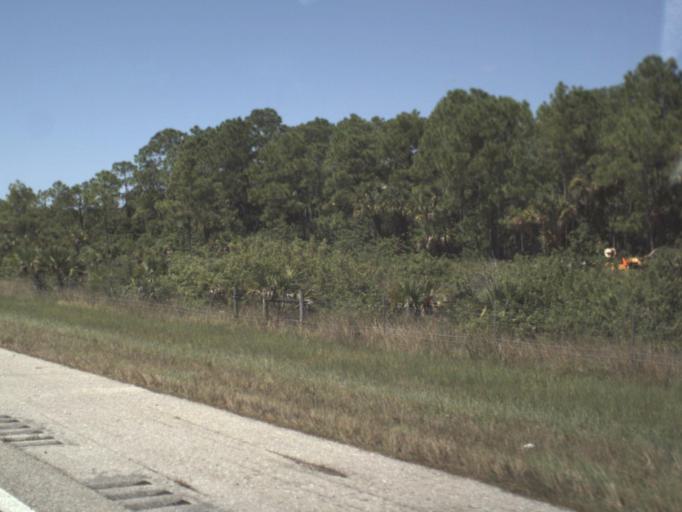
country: US
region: Florida
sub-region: Collier County
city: Orangetree
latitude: 26.1532
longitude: -81.5401
